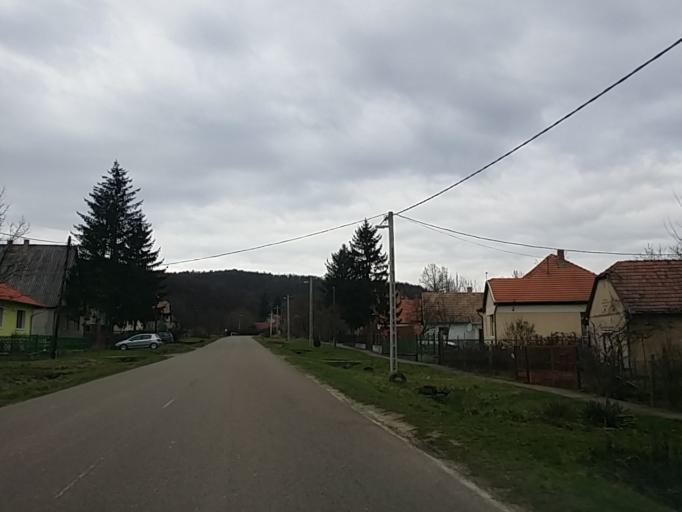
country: HU
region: Heves
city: Sirok
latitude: 47.8979
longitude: 20.1815
